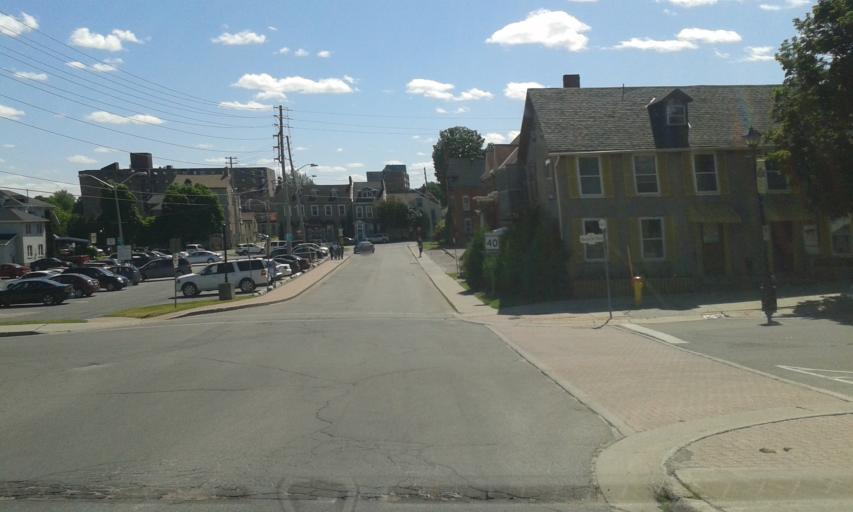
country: CA
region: Ontario
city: Brockville
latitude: 44.5897
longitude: -75.6820
